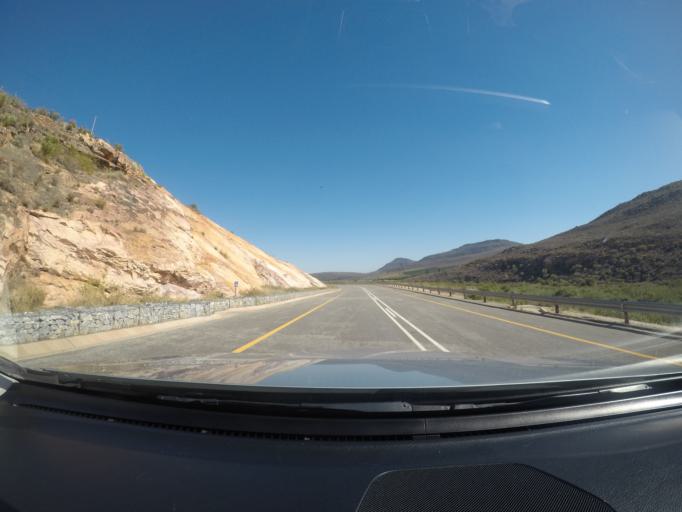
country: ZA
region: Western Cape
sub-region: West Coast District Municipality
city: Clanwilliam
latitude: -32.4038
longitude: 18.9548
